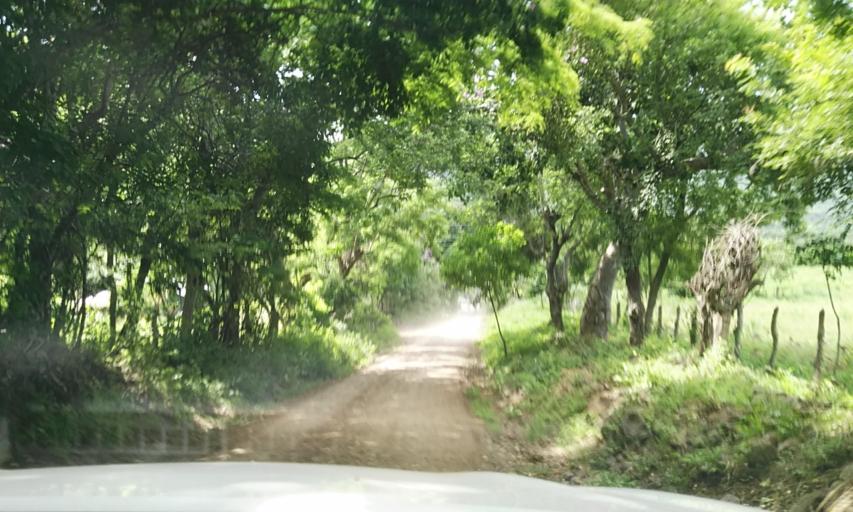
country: NI
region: Matagalpa
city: Terrabona
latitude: 12.7047
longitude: -85.9481
